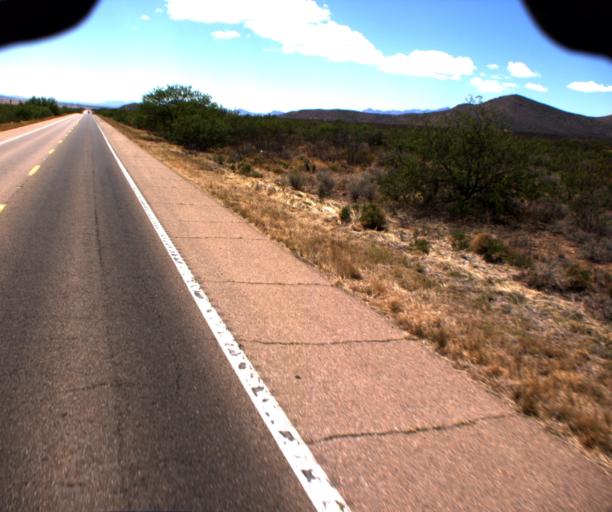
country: US
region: Arizona
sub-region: Cochise County
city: Naco
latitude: 31.3872
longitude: -109.9474
